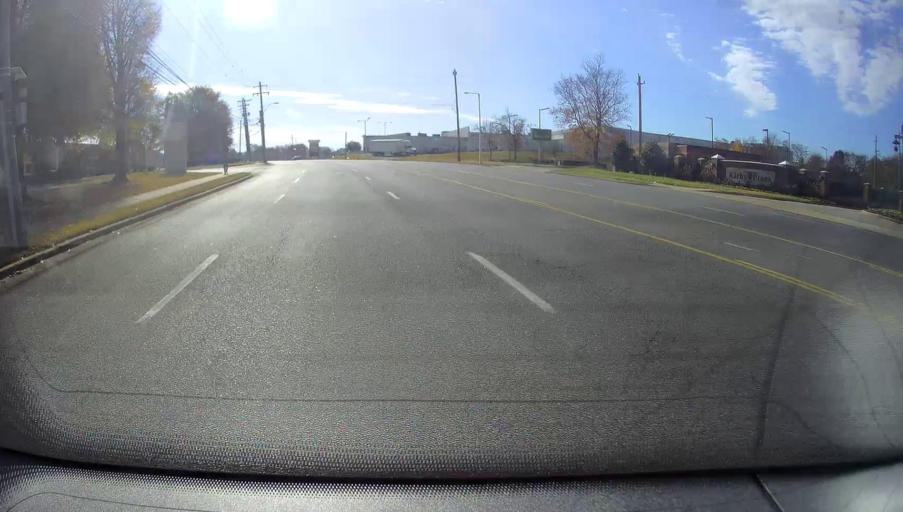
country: US
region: Tennessee
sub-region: Shelby County
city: Germantown
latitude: 35.0535
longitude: -89.8441
